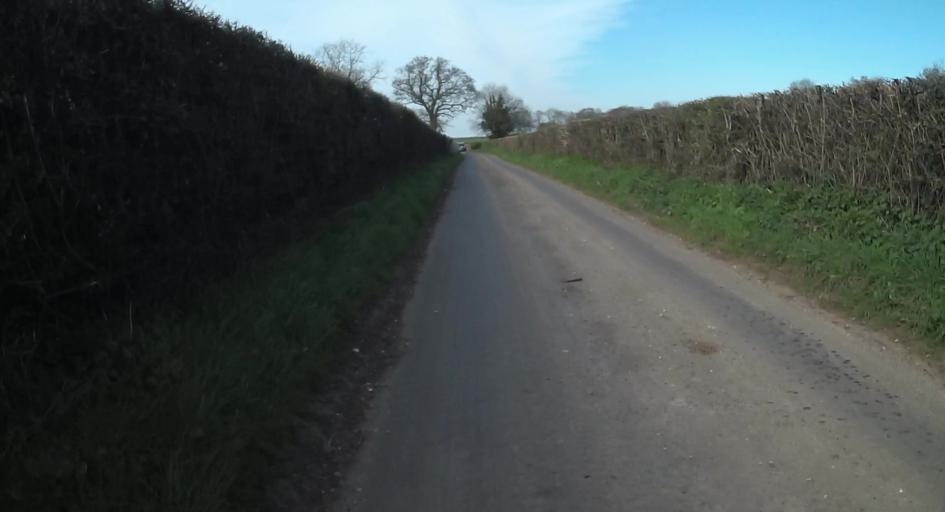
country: GB
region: England
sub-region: Hampshire
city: Old Basing
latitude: 51.2342
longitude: -1.0376
